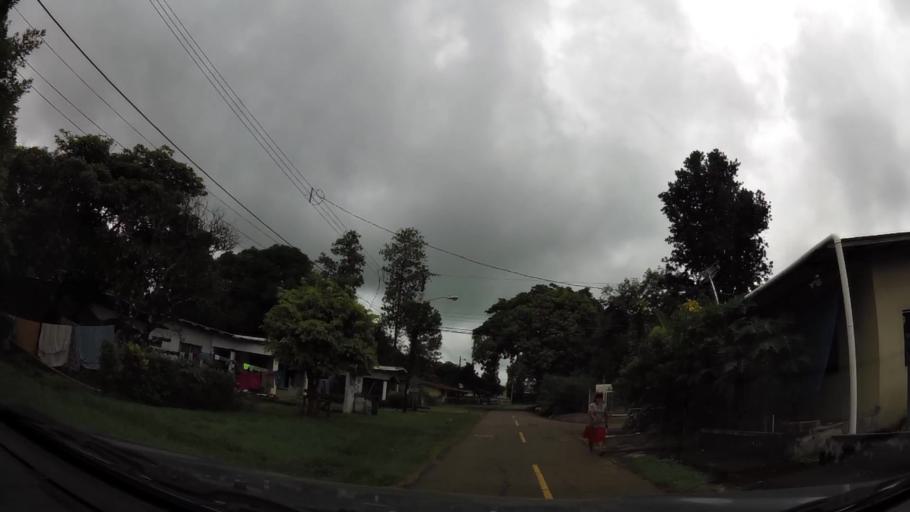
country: PA
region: Chiriqui
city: Dolega District
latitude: 8.5615
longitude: -82.4146
